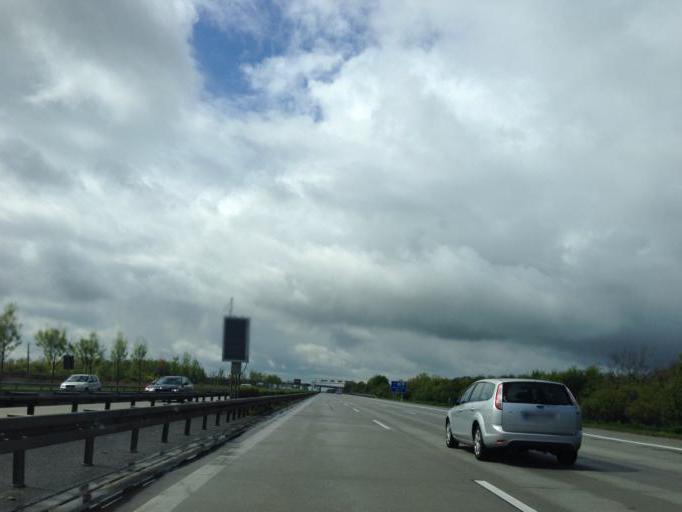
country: DE
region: Saxony
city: Rackwitz
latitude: 51.4090
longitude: 12.3723
